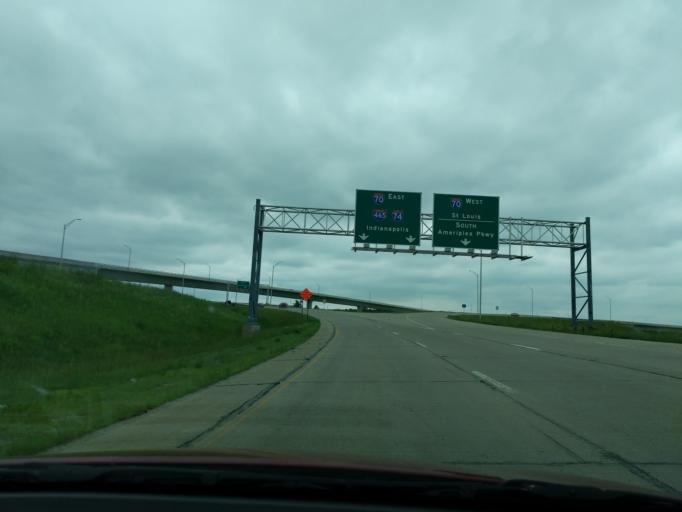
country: US
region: Indiana
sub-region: Hendricks County
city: Plainfield
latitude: 39.6939
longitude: -86.3196
